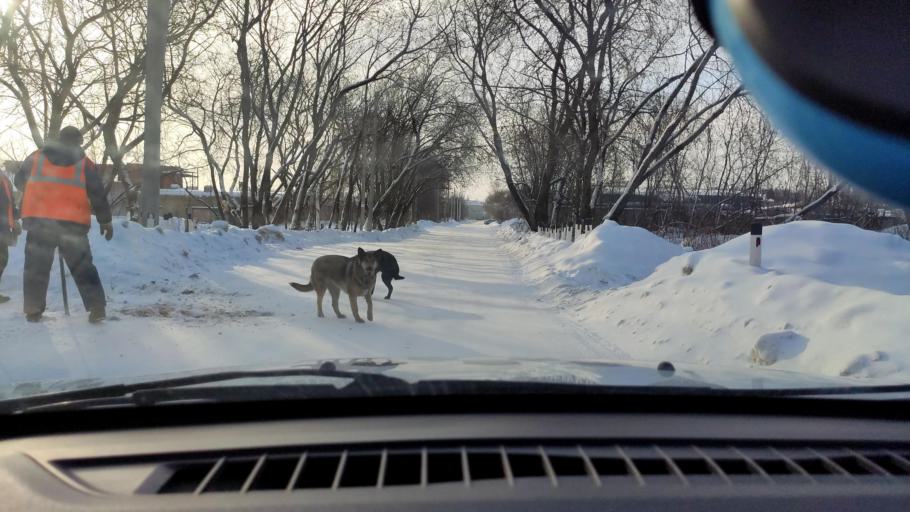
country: RU
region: Perm
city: Kultayevo
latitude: 57.9960
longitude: 55.9252
